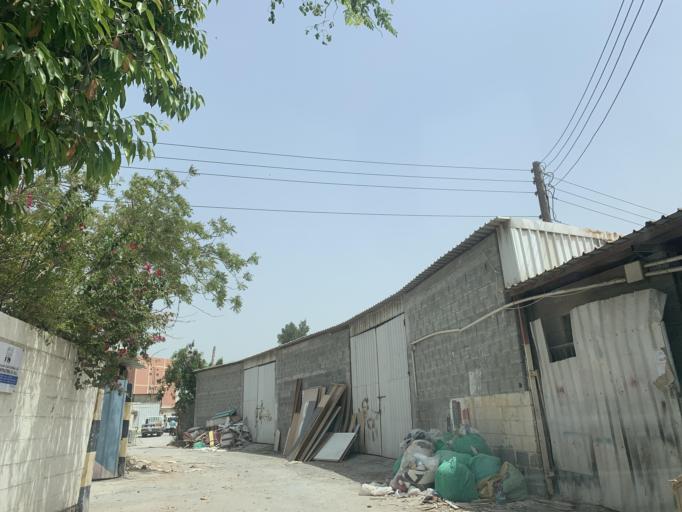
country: BH
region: Northern
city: Madinat `Isa
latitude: 26.1805
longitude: 50.5579
